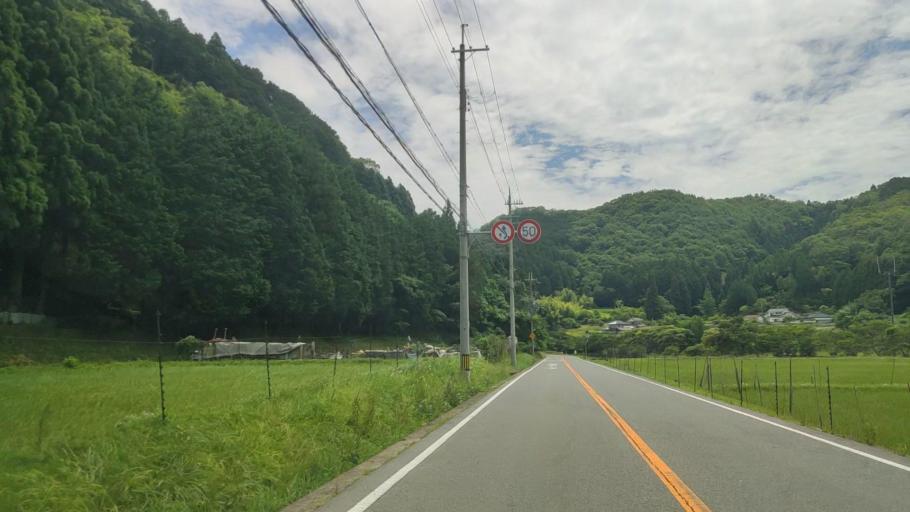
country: JP
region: Hyogo
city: Yamazakicho-nakabirose
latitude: 35.0845
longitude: 134.3585
